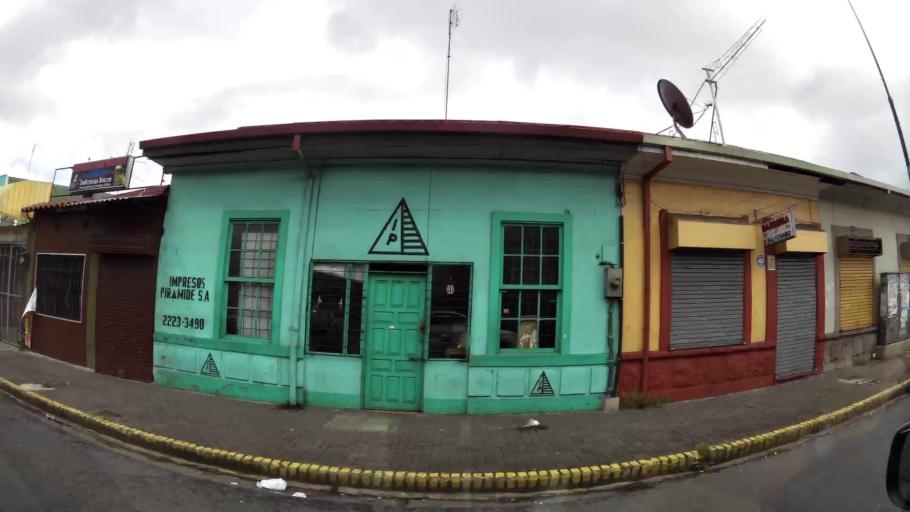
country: CR
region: San Jose
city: San Jose
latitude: 9.9277
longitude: -84.0756
